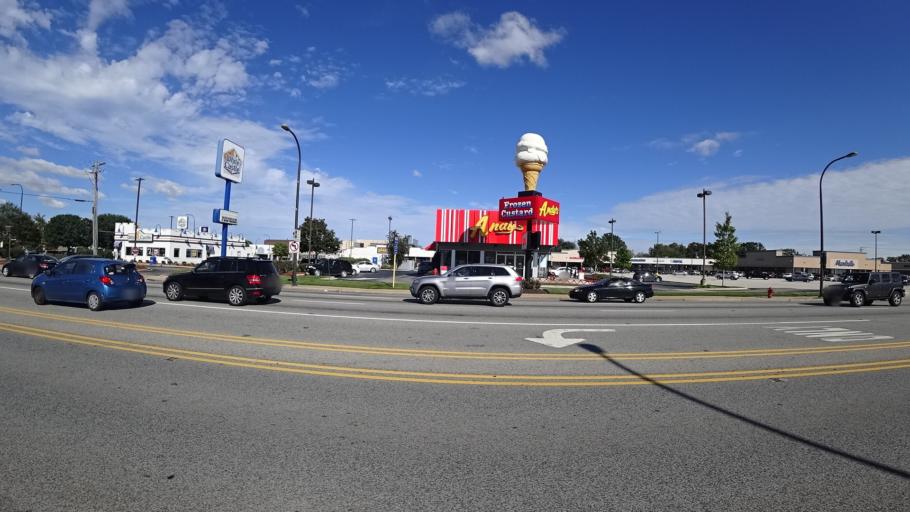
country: US
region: Illinois
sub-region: Cook County
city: Hometown
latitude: 41.7194
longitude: -87.7409
